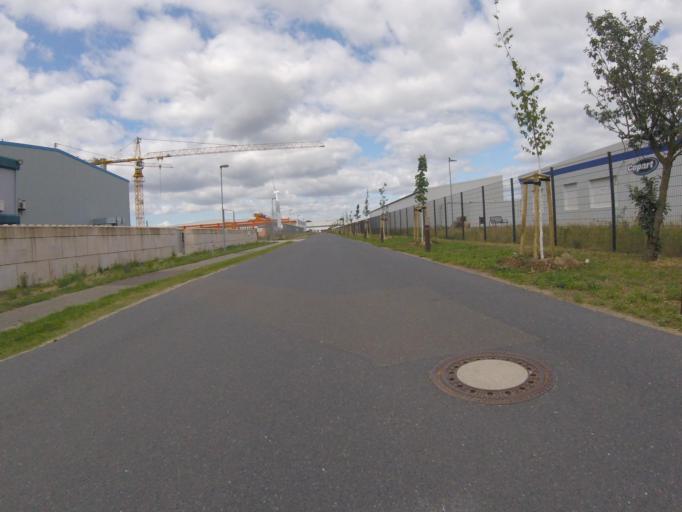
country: DE
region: Brandenburg
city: Wildau
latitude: 52.3187
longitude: 13.6722
